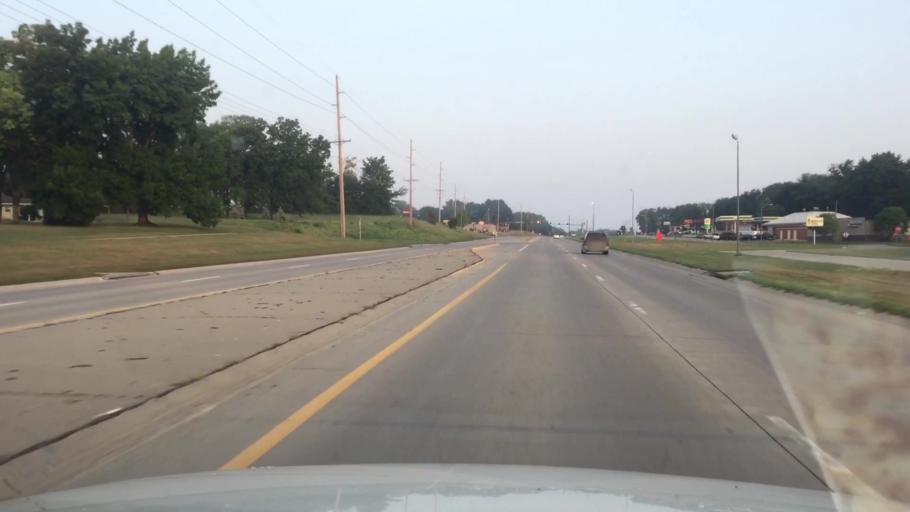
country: US
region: Iowa
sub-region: Warren County
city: Carlisle
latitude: 41.4970
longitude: -93.4934
